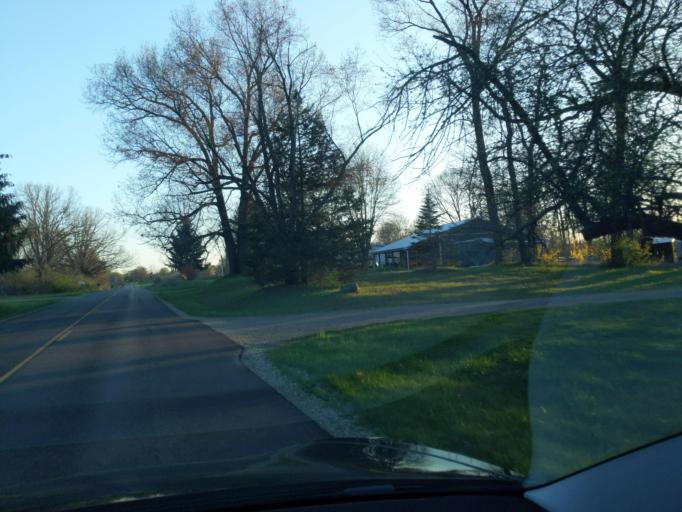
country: US
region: Michigan
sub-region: Ingham County
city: Stockbridge
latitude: 42.4943
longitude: -84.2871
